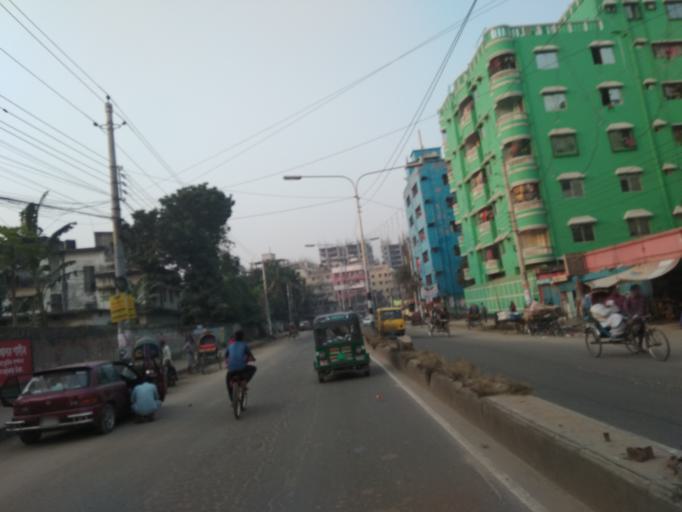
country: BD
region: Dhaka
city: Azimpur
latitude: 23.8103
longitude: 90.3610
